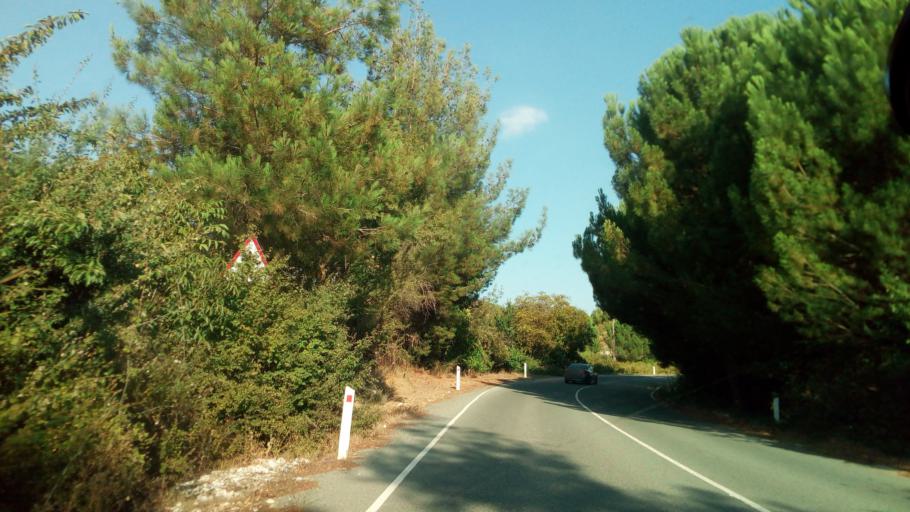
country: CY
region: Limassol
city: Pachna
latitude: 34.8686
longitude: 32.8421
